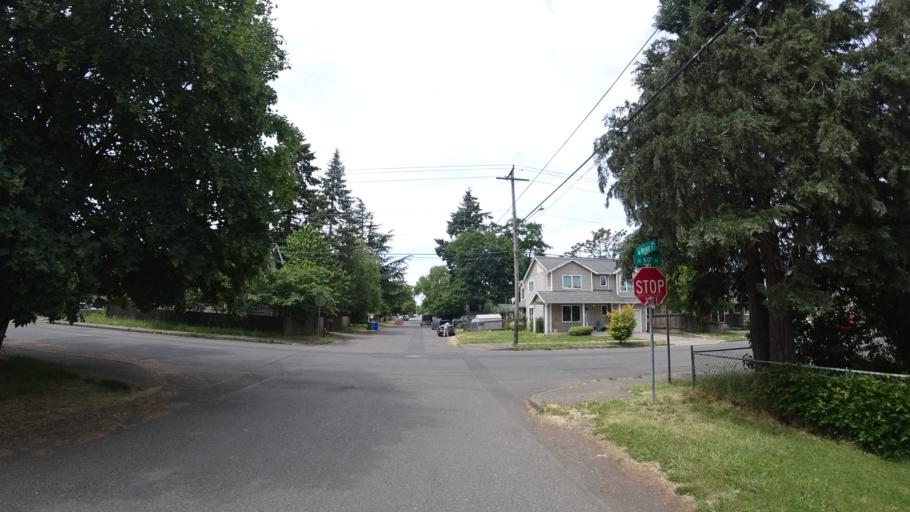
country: US
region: Oregon
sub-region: Multnomah County
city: Lents
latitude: 45.4700
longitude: -122.6020
